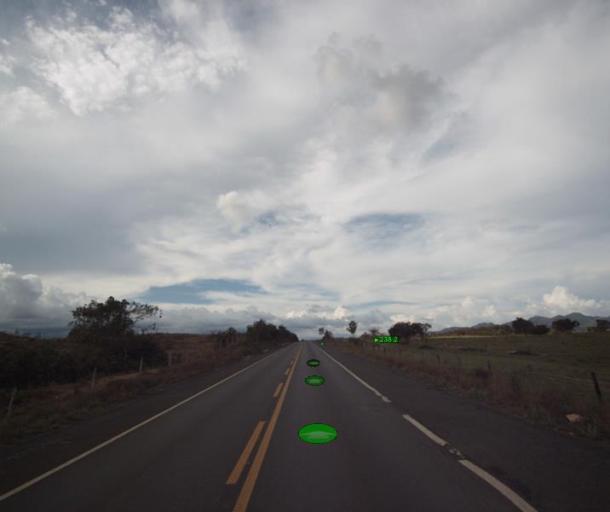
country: BR
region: Goias
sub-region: Niquelandia
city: Niquelandia
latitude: -14.7255
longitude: -48.6103
